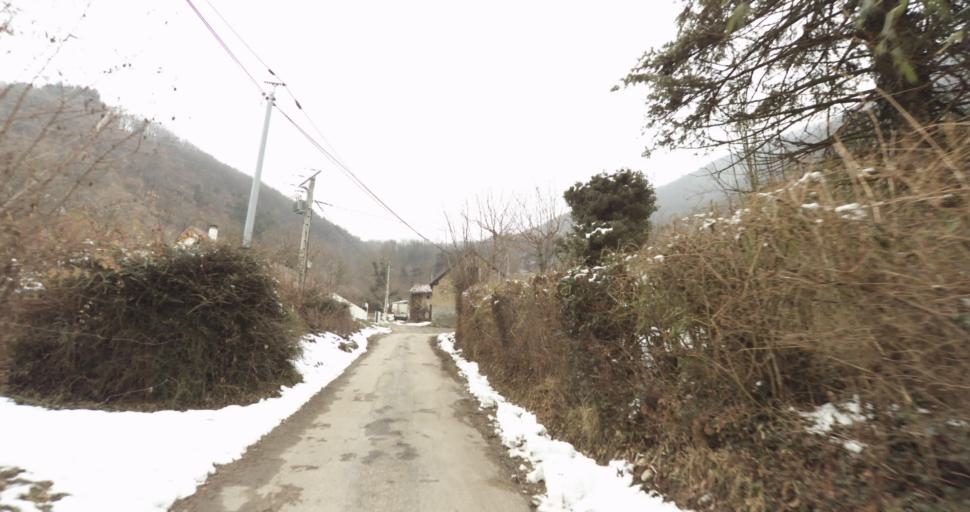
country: FR
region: Rhone-Alpes
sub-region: Departement de l'Isere
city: Vif
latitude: 45.0190
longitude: 5.6692
